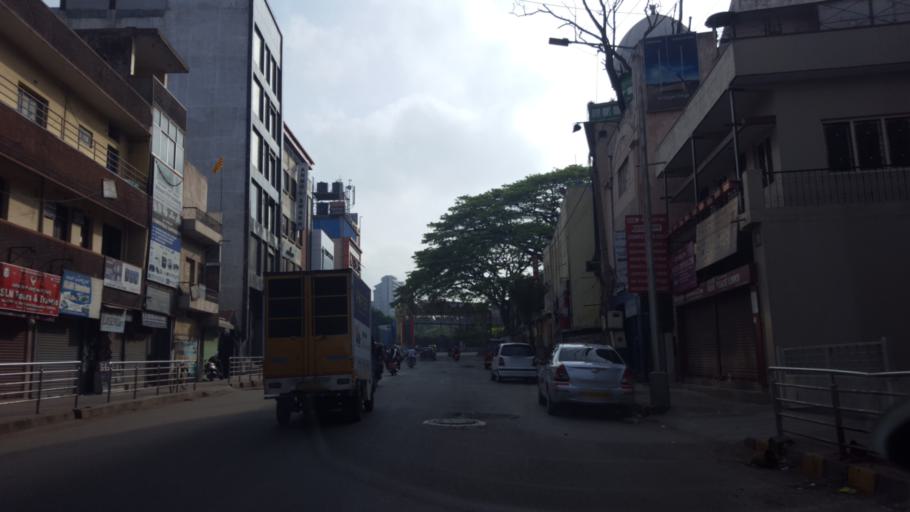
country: IN
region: Karnataka
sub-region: Bangalore Urban
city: Bangalore
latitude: 12.9656
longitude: 77.5852
